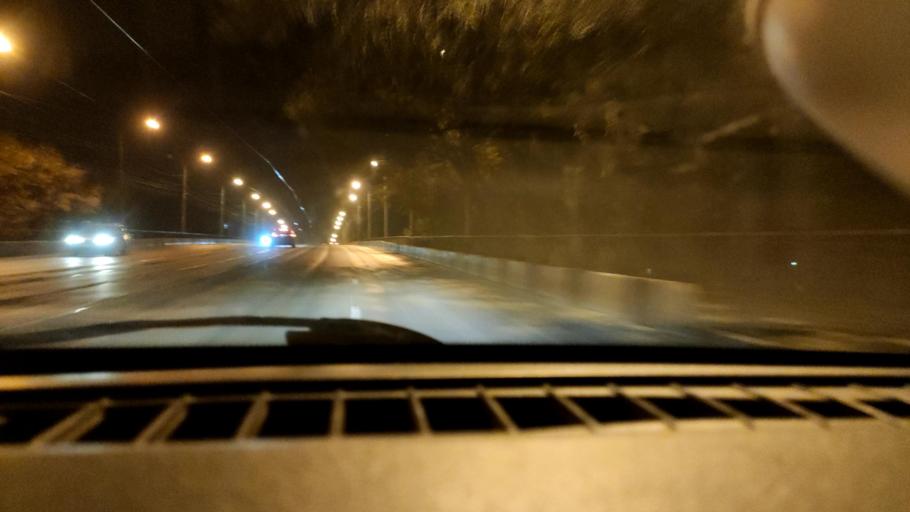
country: RU
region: Samara
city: Samara
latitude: 53.2000
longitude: 50.2438
